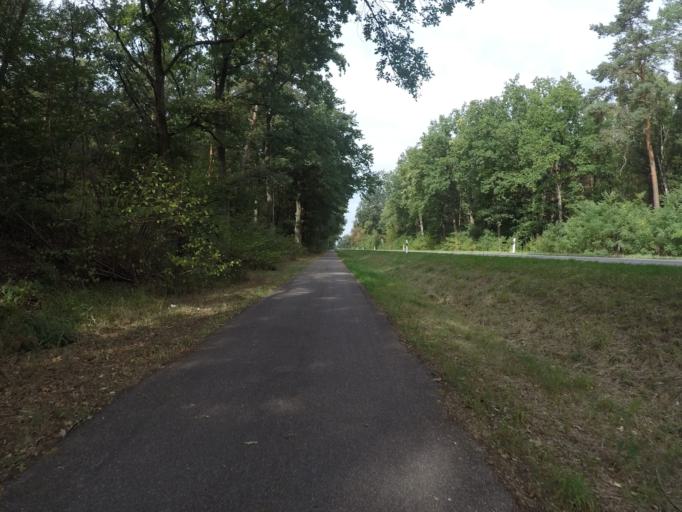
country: DE
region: Rheinland-Pfalz
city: Hanhofen
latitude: 49.3535
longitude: 8.3420
